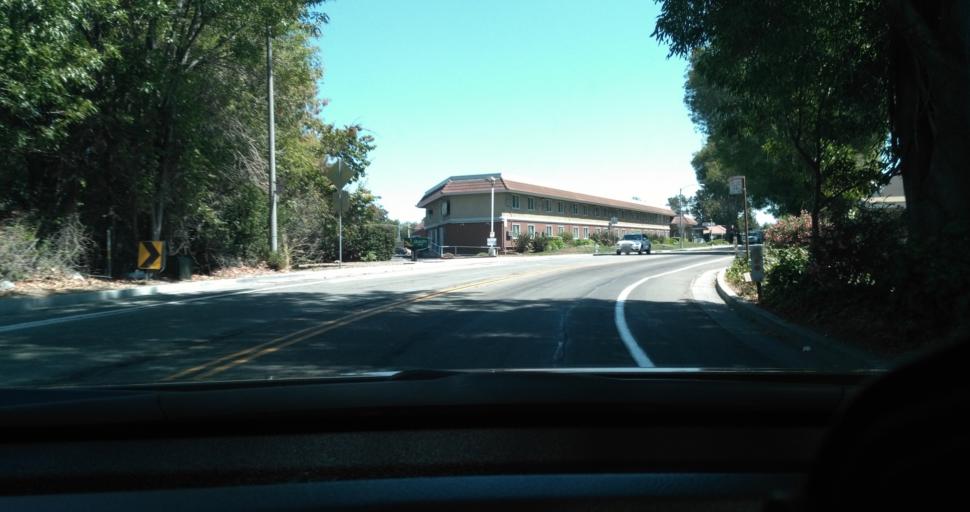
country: US
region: California
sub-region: Santa Clara County
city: Sunnyvale
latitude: 37.4079
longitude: -121.9993
